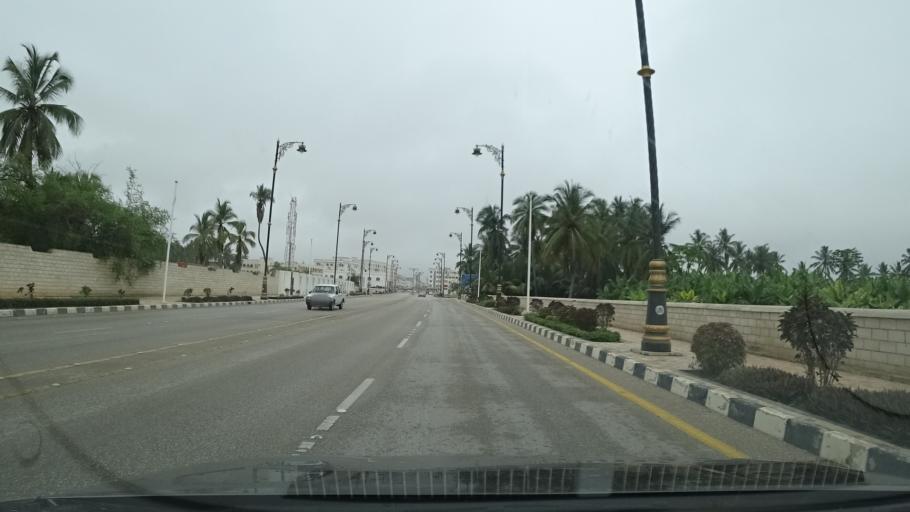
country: OM
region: Zufar
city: Salalah
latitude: 17.0070
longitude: 54.0962
